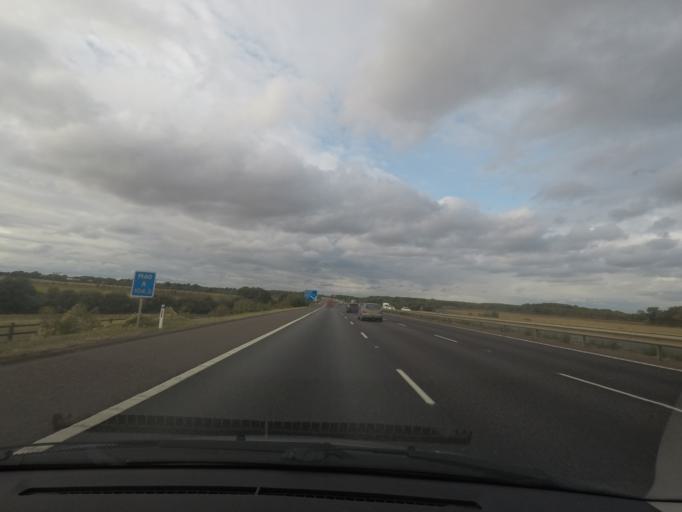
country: GB
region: England
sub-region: Oxfordshire
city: Bicester
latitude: 51.9309
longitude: -1.2020
